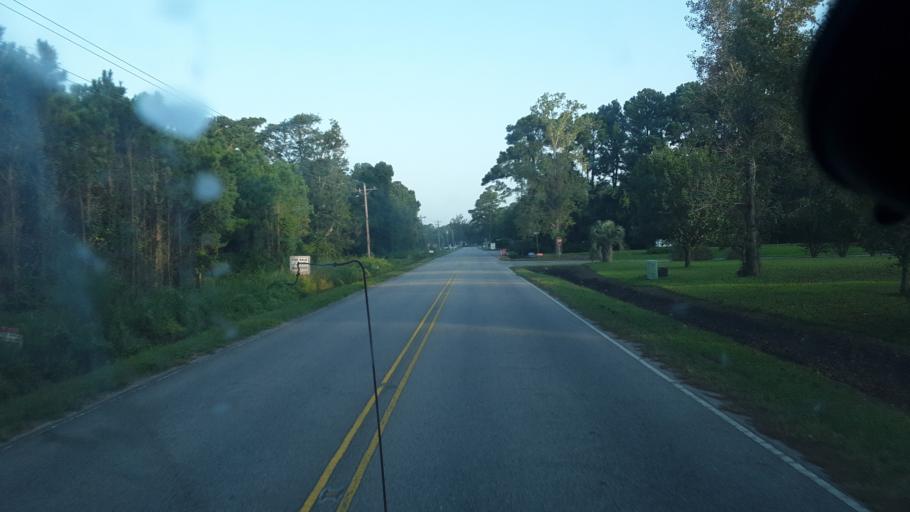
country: US
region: North Carolina
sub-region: Brunswick County
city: Calabash
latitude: 33.8805
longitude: -78.5444
